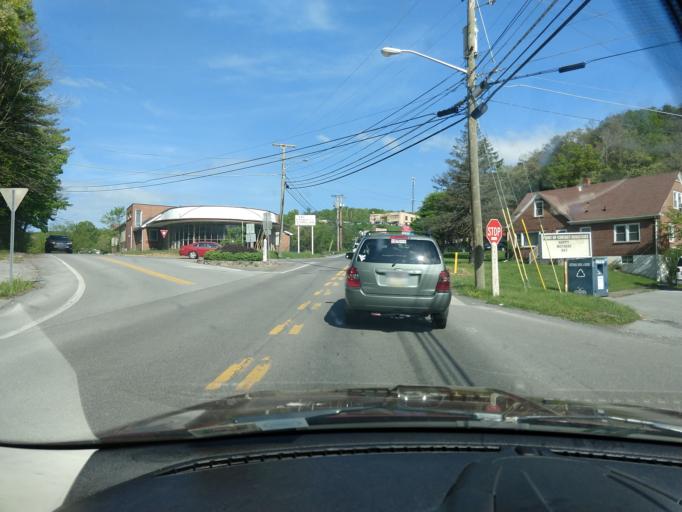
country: US
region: West Virginia
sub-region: Mercer County
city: Bluefield
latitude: 37.2541
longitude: -81.2326
